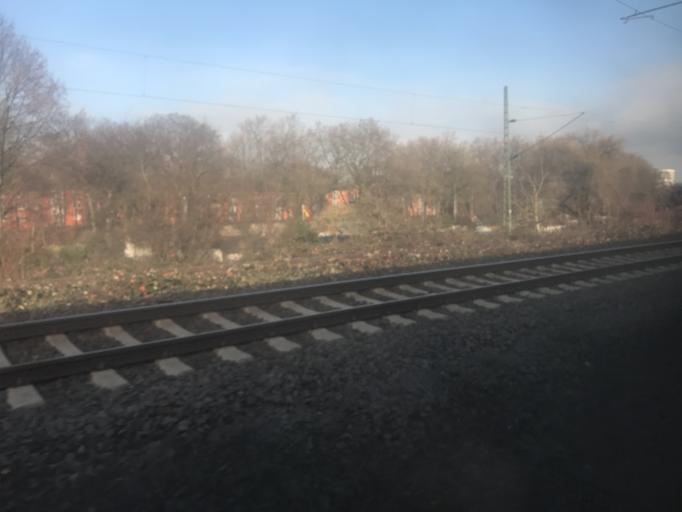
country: DE
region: North Rhine-Westphalia
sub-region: Regierungsbezirk Koln
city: Buchforst
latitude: 50.9518
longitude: 6.9982
